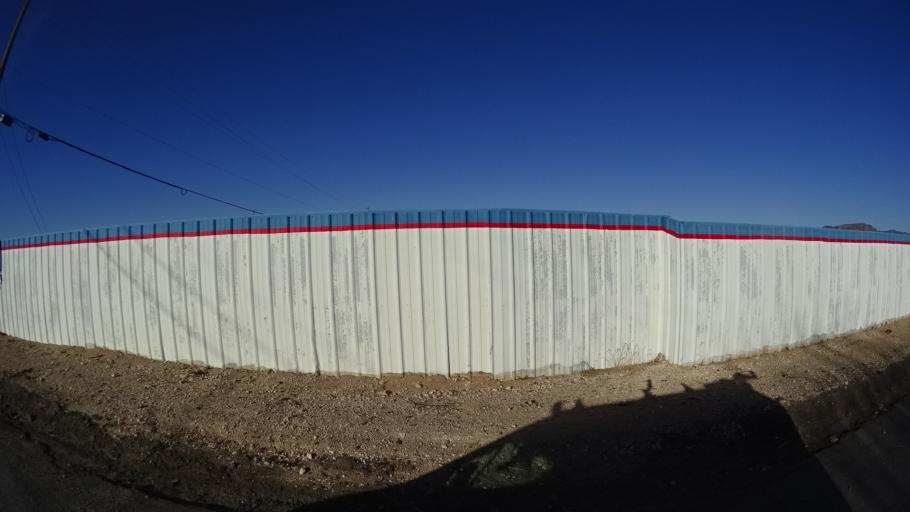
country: US
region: Arizona
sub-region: Mohave County
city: Kingman
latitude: 35.2060
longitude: -114.0158
